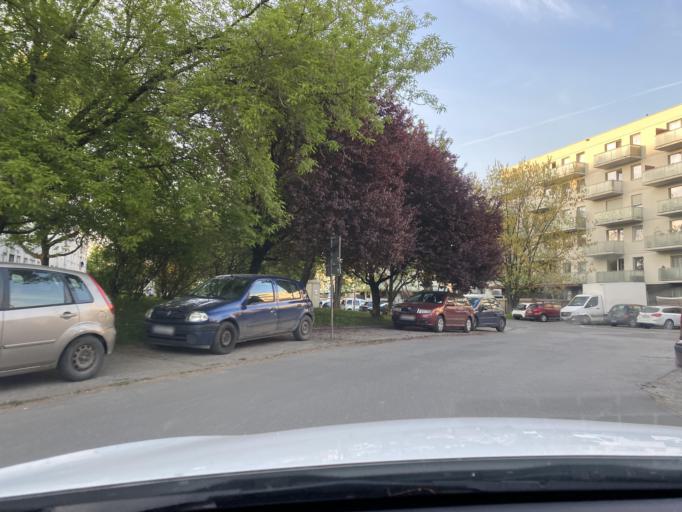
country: PL
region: Lower Silesian Voivodeship
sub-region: Powiat wroclawski
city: Wroclaw
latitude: 51.1392
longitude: 17.0254
